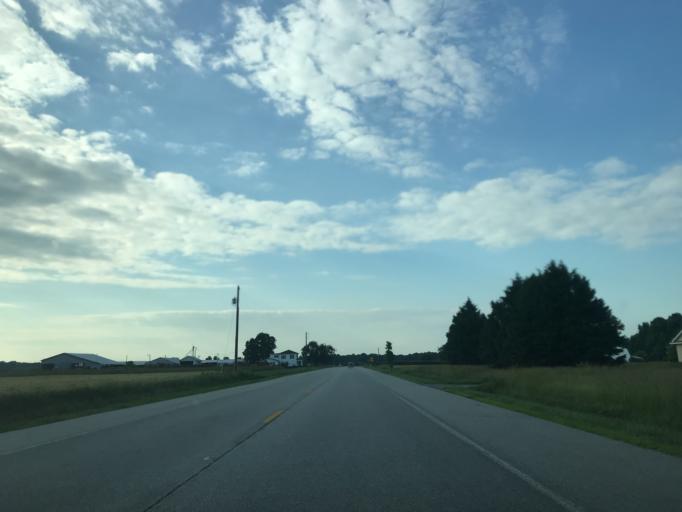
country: US
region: Maryland
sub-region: Caroline County
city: Federalsburg
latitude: 38.7403
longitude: -75.7928
